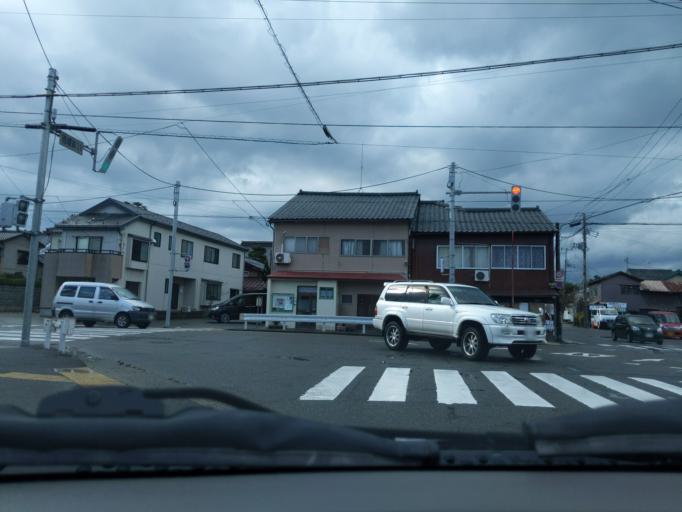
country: JP
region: Niigata
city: Niigata-shi
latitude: 37.9289
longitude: 139.0458
